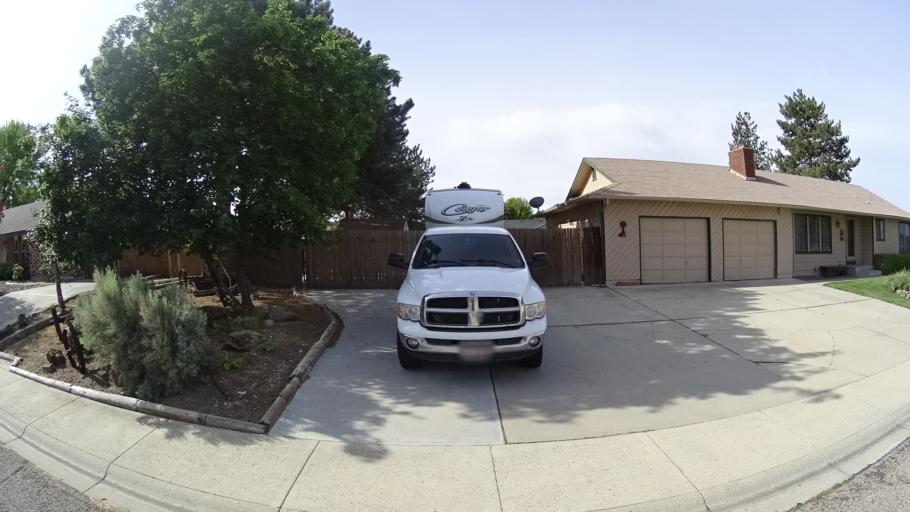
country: US
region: Idaho
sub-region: Ada County
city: Meridian
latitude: 43.5652
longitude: -116.3313
